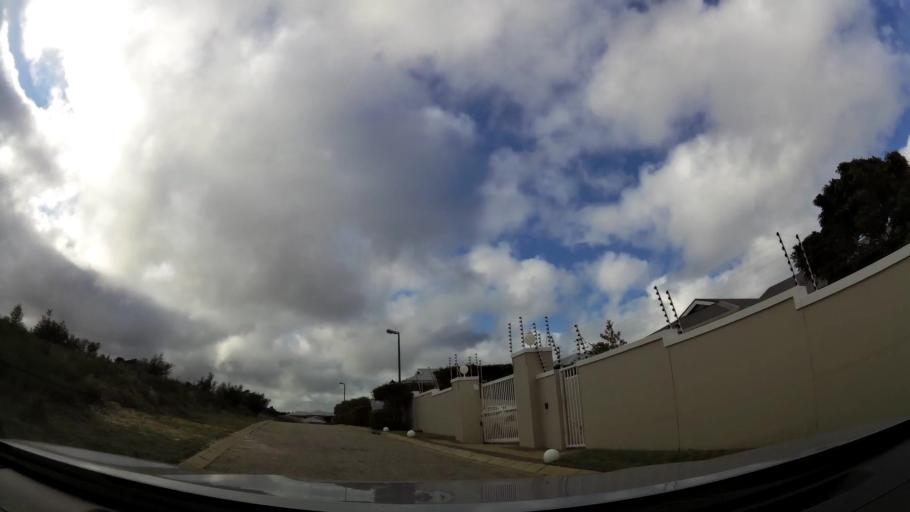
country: ZA
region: Western Cape
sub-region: Eden District Municipality
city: Plettenberg Bay
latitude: -34.0841
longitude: 23.3577
